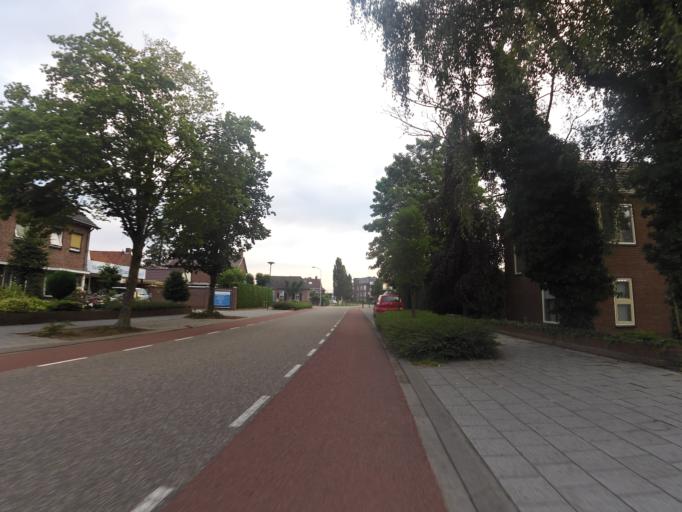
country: NL
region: Gelderland
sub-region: Oude IJsselstreek
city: Gendringen
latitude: 51.8938
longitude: 6.3789
